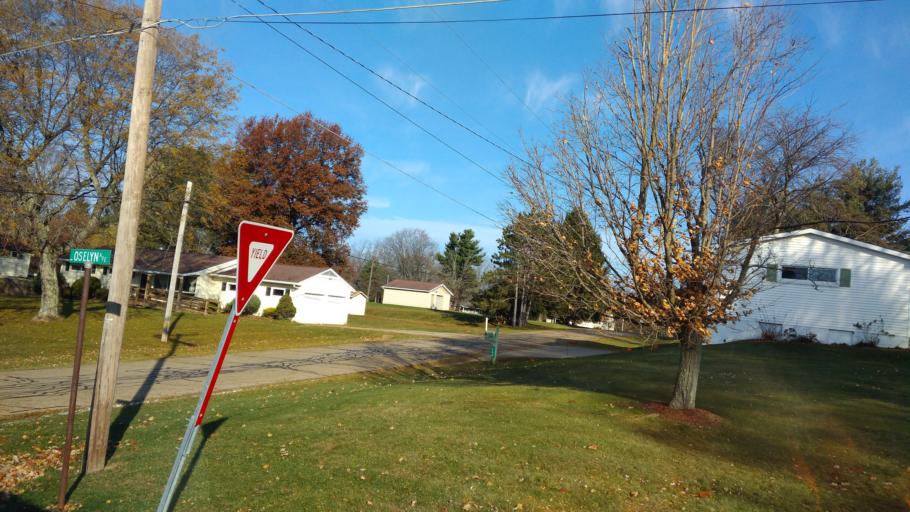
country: US
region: Ohio
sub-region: Richland County
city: Lexington
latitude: 40.6973
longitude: -82.5428
